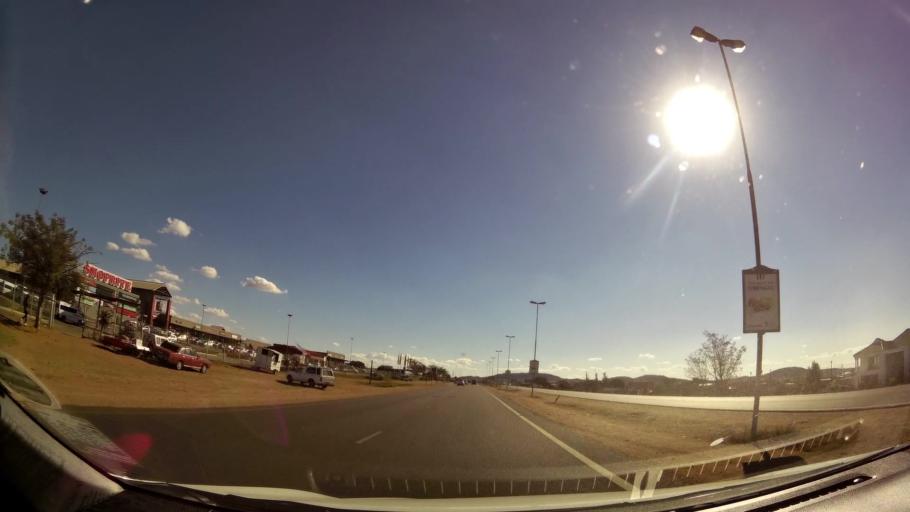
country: ZA
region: Limpopo
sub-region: Capricorn District Municipality
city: Mankoeng
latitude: -23.8898
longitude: 29.7036
